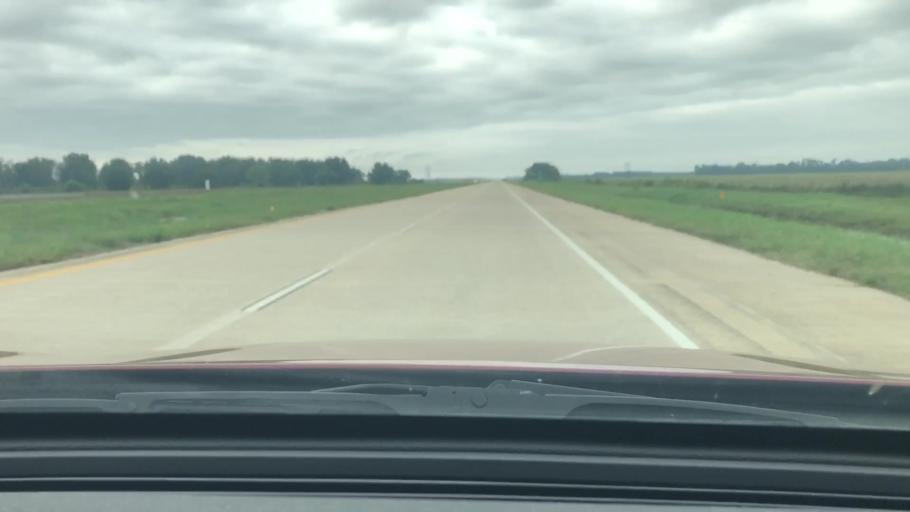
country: US
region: Louisiana
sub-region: Caddo Parish
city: Oil City
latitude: 32.7265
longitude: -93.8719
